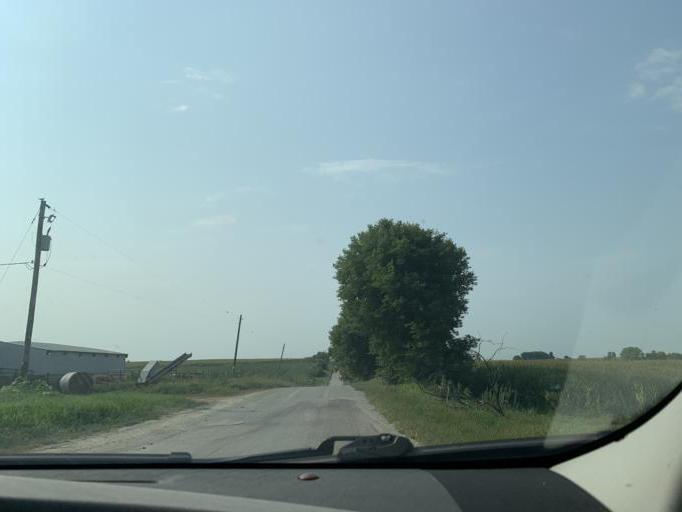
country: US
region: Illinois
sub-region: Whiteside County
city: Sterling
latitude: 41.8334
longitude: -89.7471
